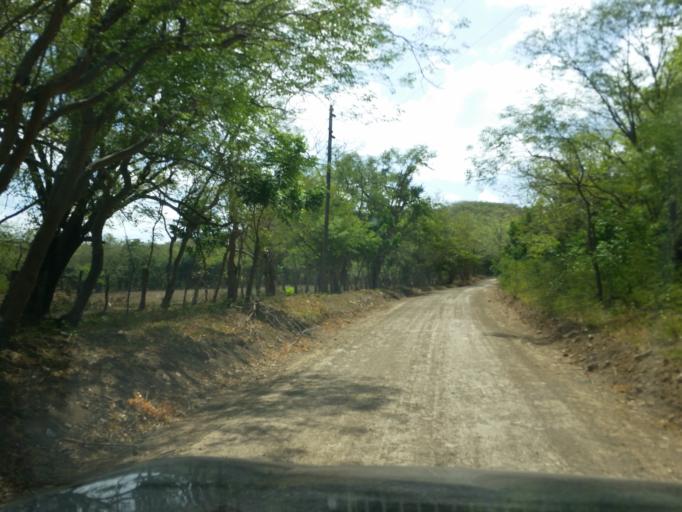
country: NI
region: Rivas
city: San Juan del Sur
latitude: 11.1358
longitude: -85.7811
